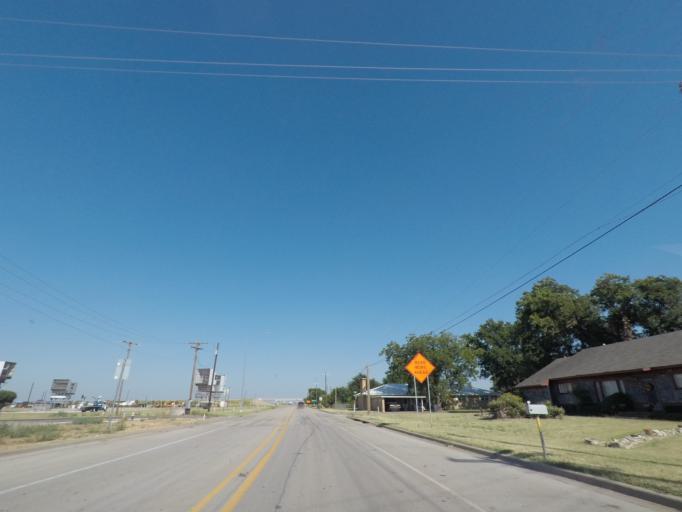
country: US
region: Texas
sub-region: Baylor County
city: Seymour
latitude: 33.5959
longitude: -99.2466
